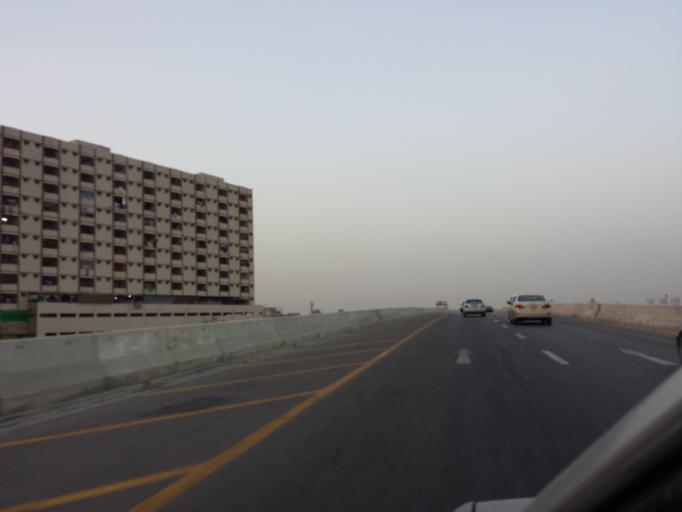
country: PK
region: Sindh
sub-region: Karachi District
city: Karachi
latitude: 24.9057
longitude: 67.0630
